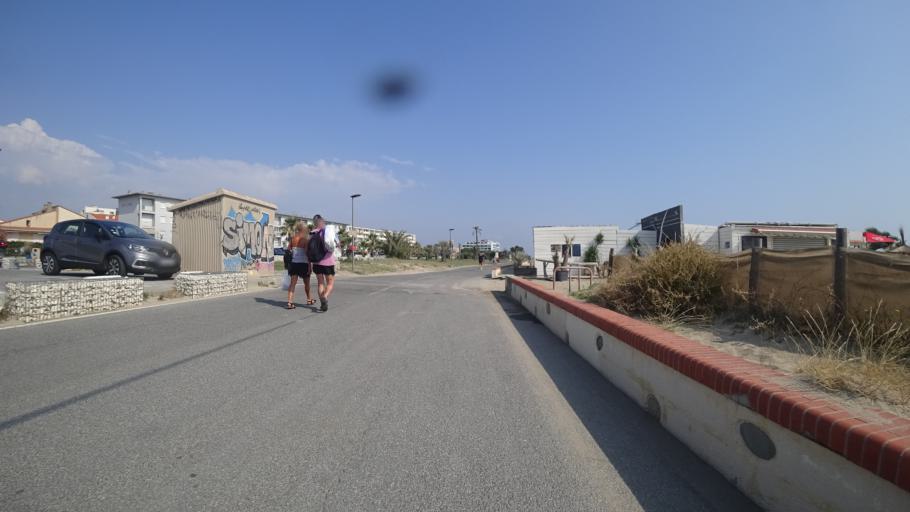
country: FR
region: Languedoc-Roussillon
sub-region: Departement des Pyrenees-Orientales
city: Saint-Cyprien-Plage
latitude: 42.6345
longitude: 3.0351
